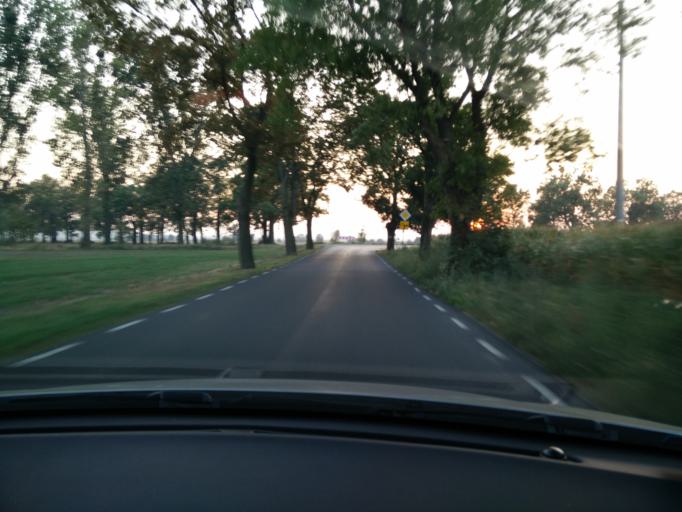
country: PL
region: Greater Poland Voivodeship
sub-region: Powiat sredzki
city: Sroda Wielkopolska
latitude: 52.2106
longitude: 17.3485
